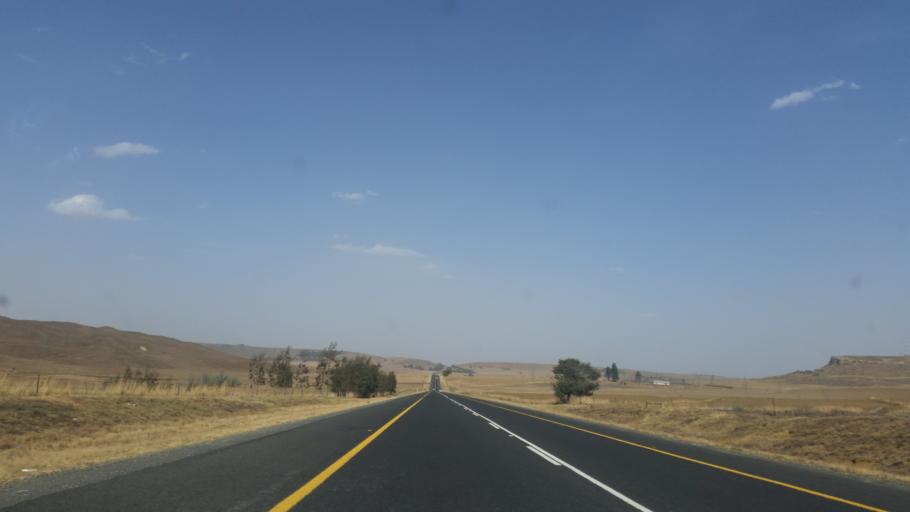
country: ZA
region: Orange Free State
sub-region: Thabo Mofutsanyana District Municipality
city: Phuthaditjhaba
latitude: -28.2813
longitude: 28.6353
